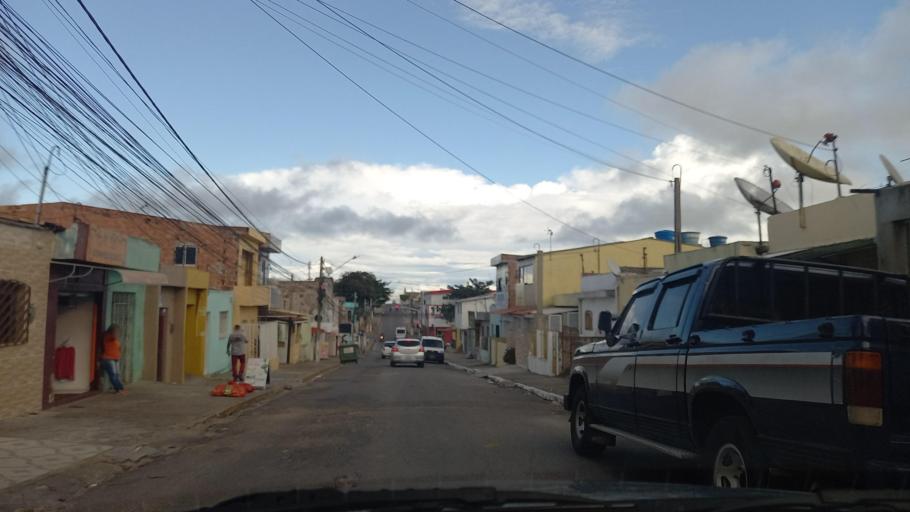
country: BR
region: Pernambuco
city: Garanhuns
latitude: -8.9002
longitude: -36.4943
